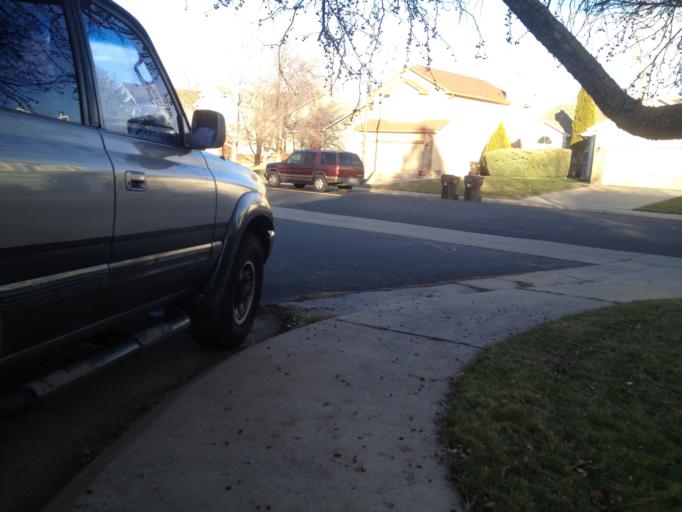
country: US
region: Colorado
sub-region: Boulder County
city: Superior
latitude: 39.9660
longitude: -105.1598
